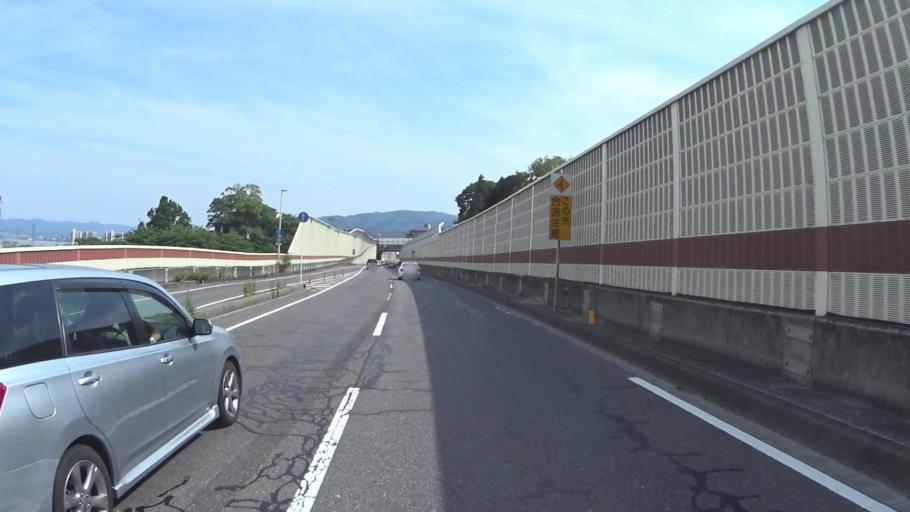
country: JP
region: Shiga Prefecture
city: Otsu-shi
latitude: 35.0386
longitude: 135.8526
